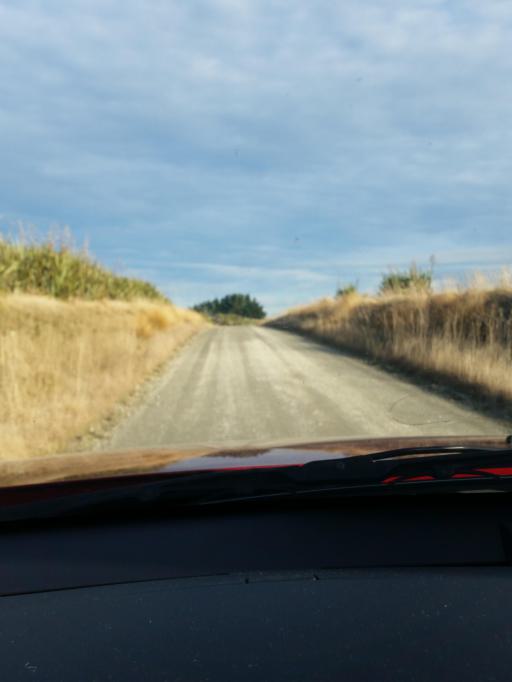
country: NZ
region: Southland
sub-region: Gore District
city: Gore
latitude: -46.2298
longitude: 168.7712
